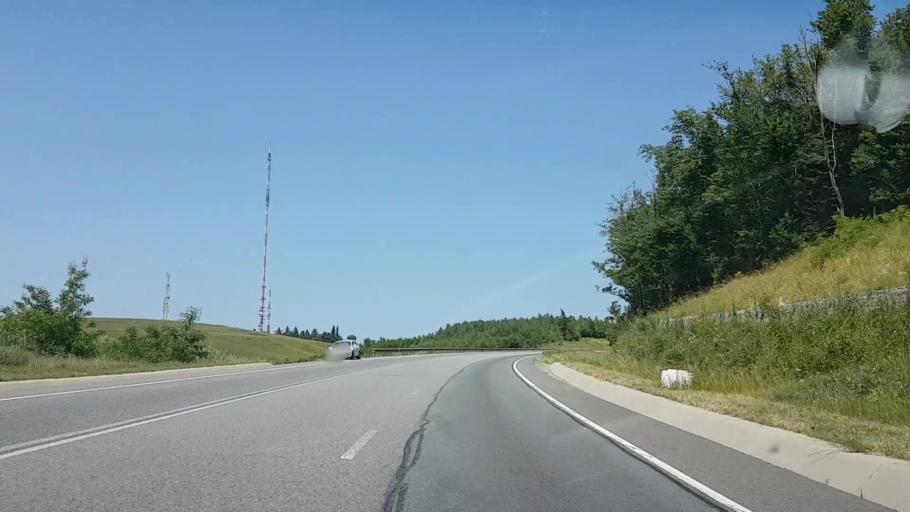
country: RO
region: Cluj
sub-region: Comuna Feleacu
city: Feleacu
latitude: 46.7055
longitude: 23.6425
